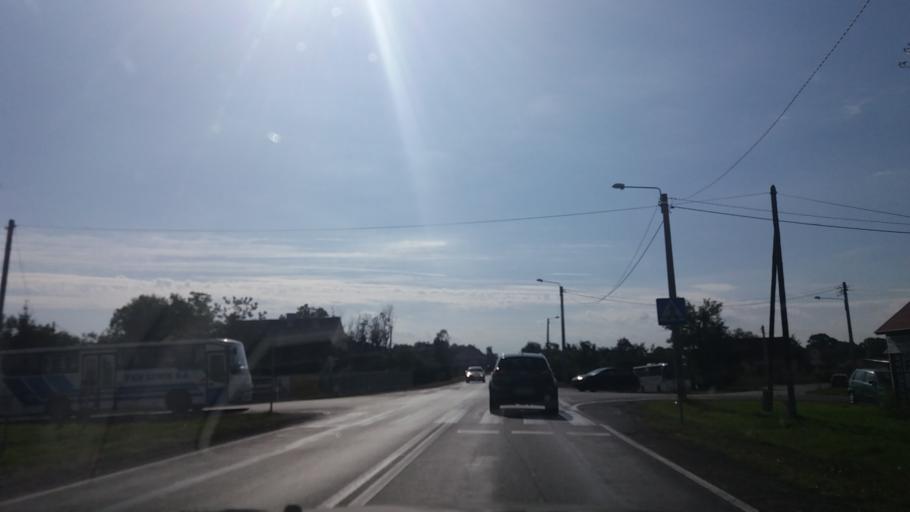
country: PL
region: Lower Silesian Voivodeship
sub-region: Powiat legnicki
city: Prochowice
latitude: 51.2888
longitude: 16.3469
